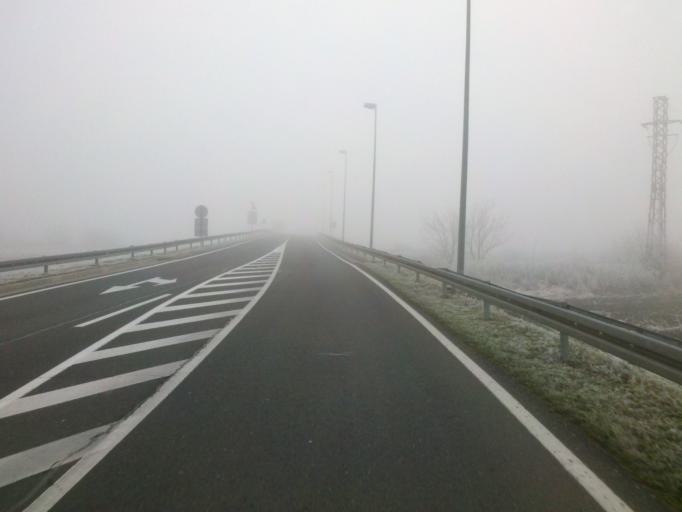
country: HR
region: Varazdinska
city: Jalkovec
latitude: 46.2921
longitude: 16.3072
